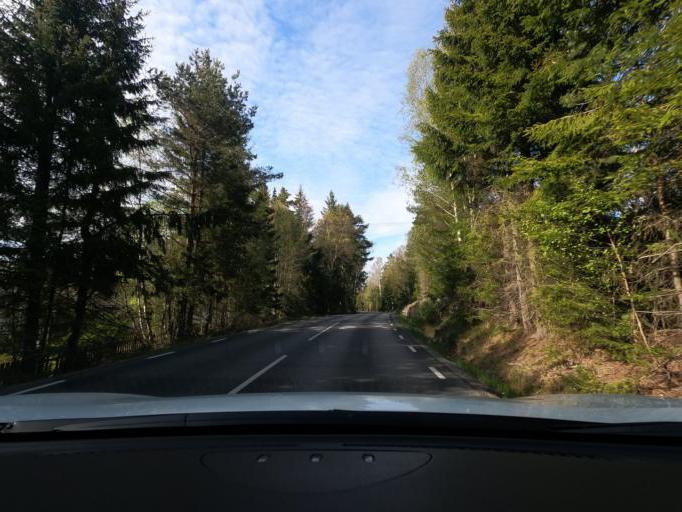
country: SE
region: Vaestra Goetaland
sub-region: Harryda Kommun
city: Landvetter
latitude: 57.6634
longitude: 12.2480
